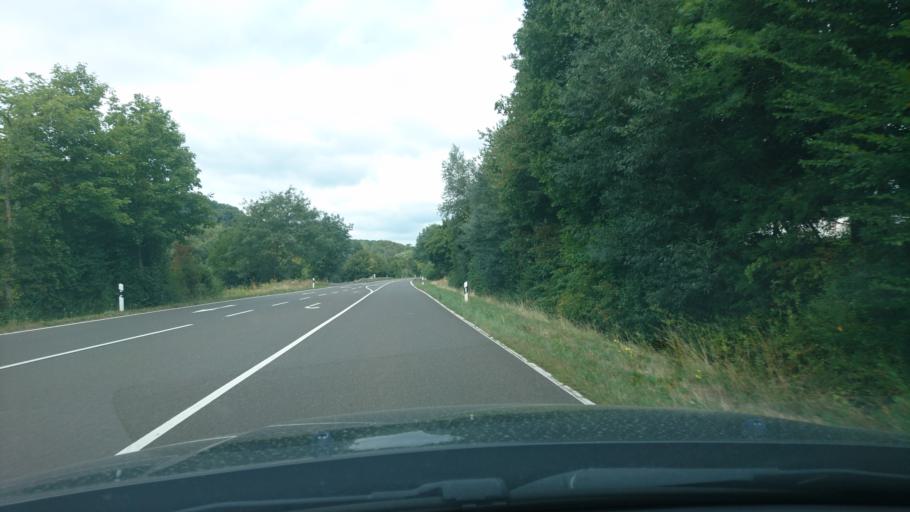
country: DE
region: Rheinland-Pfalz
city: Wiltingen
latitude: 49.6567
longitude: 6.5880
